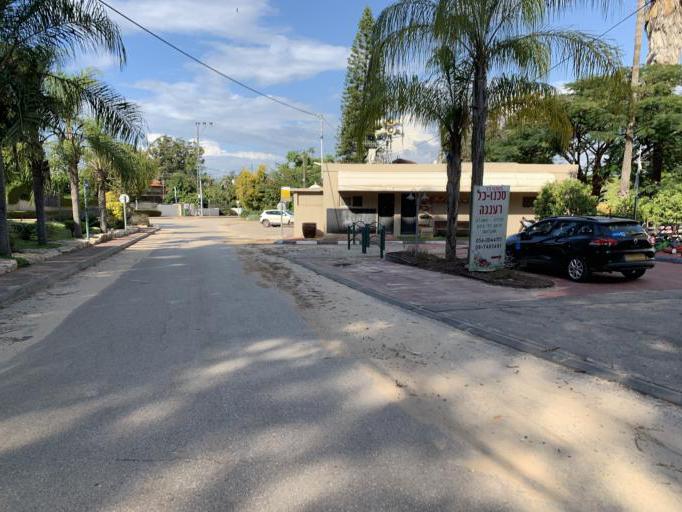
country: IL
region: Central District
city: Ra'anana
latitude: 32.1679
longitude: 34.8758
